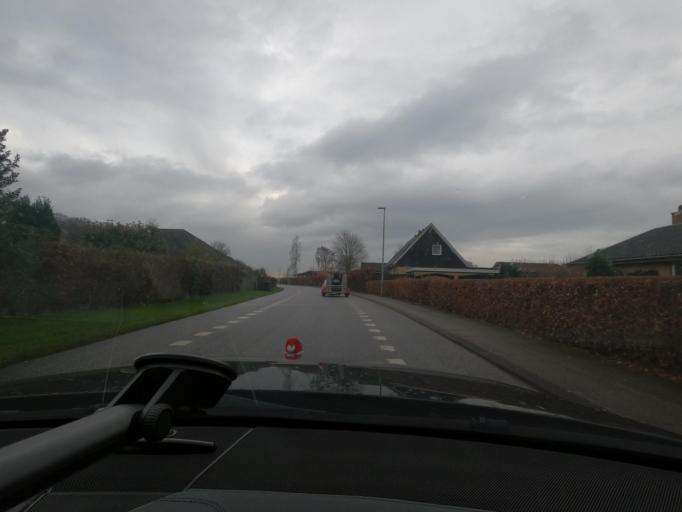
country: DK
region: South Denmark
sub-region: Sonderborg Kommune
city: Horuphav
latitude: 54.9135
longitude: 9.8938
